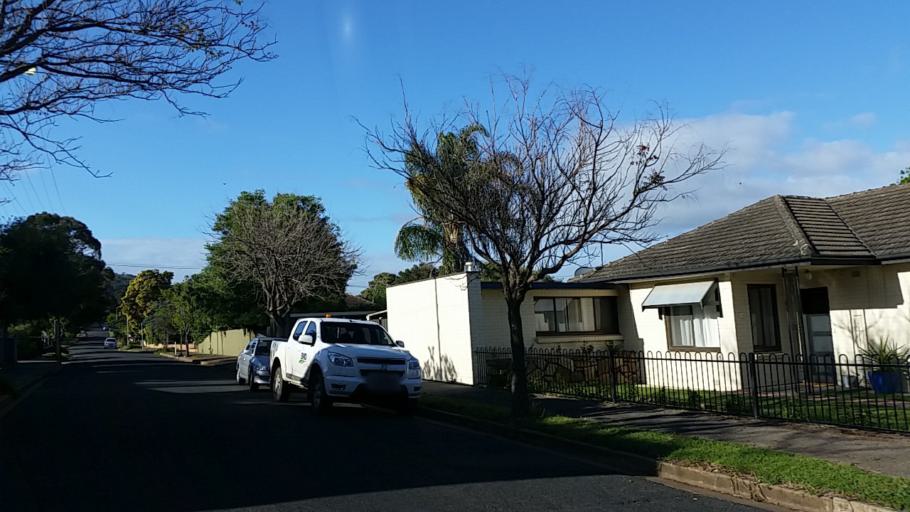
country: AU
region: South Australia
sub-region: Mitcham
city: Clapham
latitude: -34.9854
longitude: 138.6034
